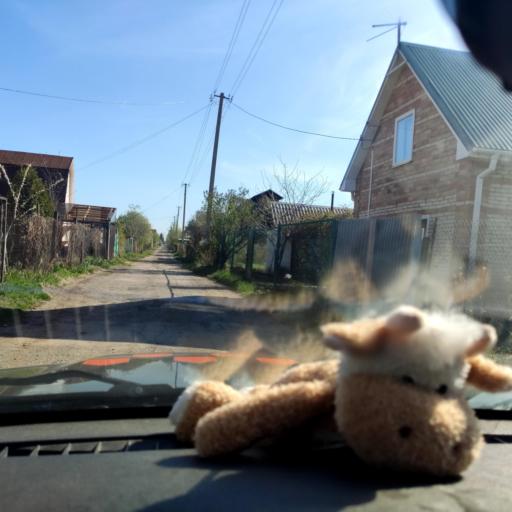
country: RU
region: Samara
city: Tol'yatti
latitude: 53.6012
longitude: 49.2657
